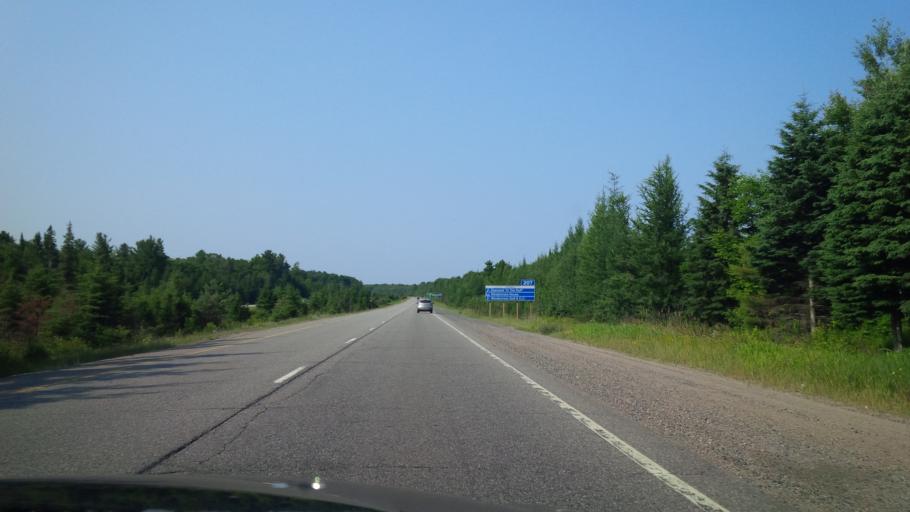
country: CA
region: Ontario
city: Huntsville
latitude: 45.2328
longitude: -79.3051
